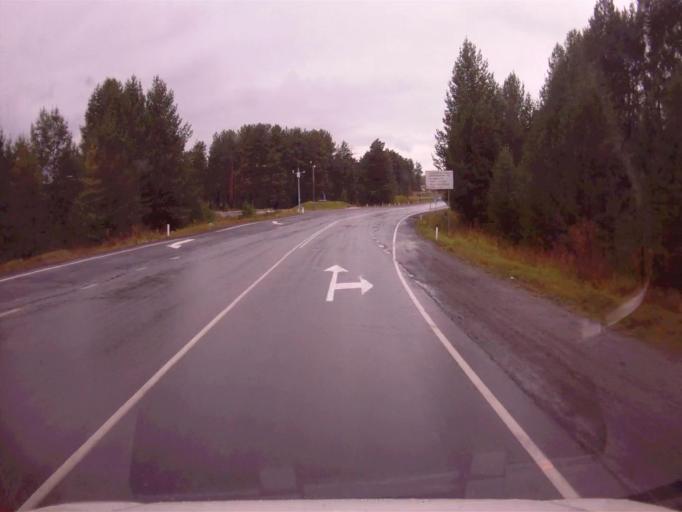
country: RU
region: Chelyabinsk
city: Verkhniy Ufaley
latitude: 56.0278
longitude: 60.2875
